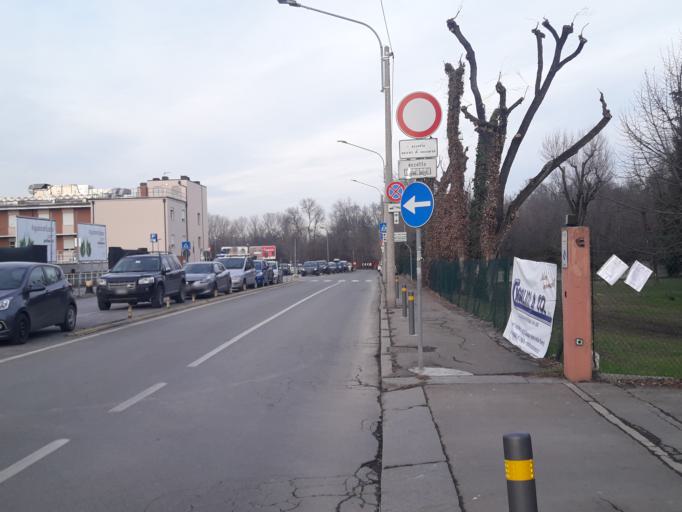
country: IT
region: Emilia-Romagna
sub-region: Provincia di Bologna
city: Bologna
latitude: 44.5048
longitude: 11.3164
